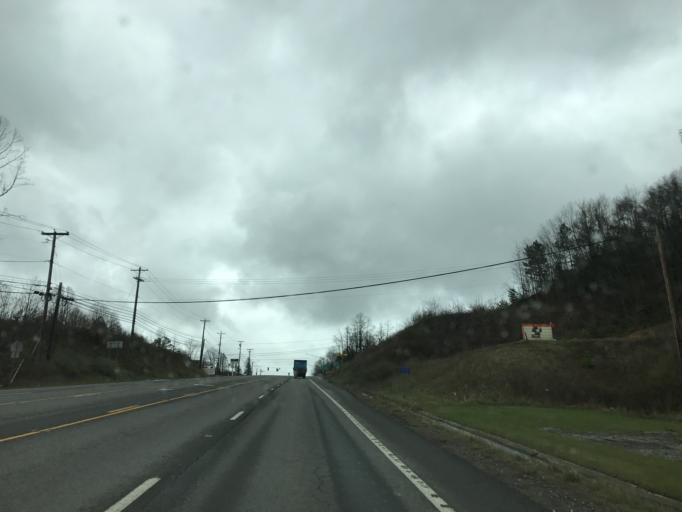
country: US
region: West Virginia
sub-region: Raleigh County
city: Prosperity
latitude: 37.8451
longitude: -81.1948
